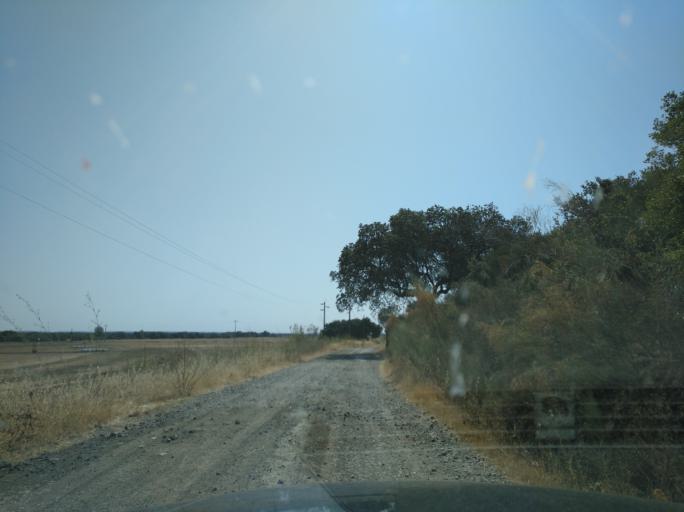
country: PT
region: Portalegre
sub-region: Campo Maior
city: Campo Maior
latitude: 39.0524
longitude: -7.0008
